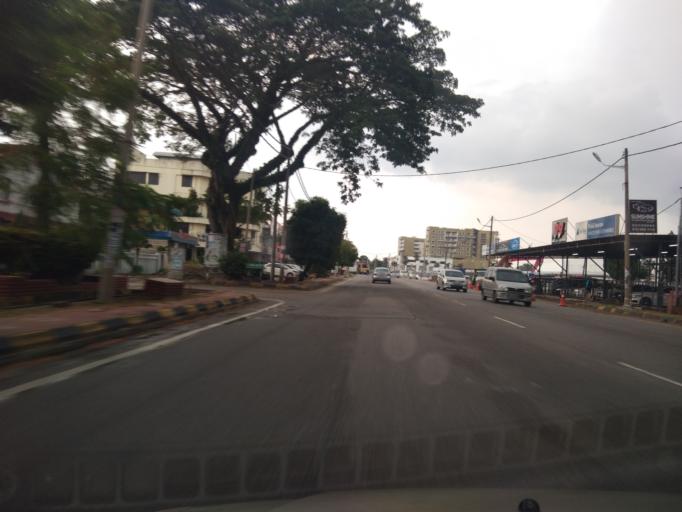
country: MY
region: Penang
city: Permatang Kuching
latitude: 5.4381
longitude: 100.3809
